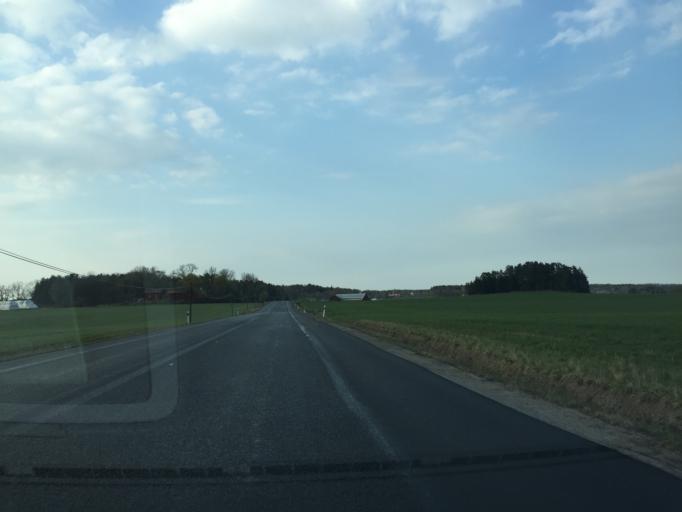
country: SE
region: Soedermanland
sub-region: Trosa Kommun
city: Vagnharad
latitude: 59.0258
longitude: 17.5949
